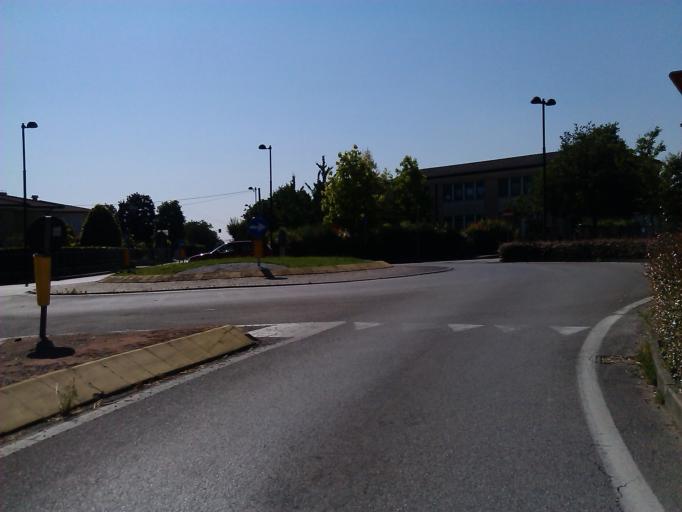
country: IT
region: Veneto
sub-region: Provincia di Vicenza
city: Cassola
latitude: 45.7514
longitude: 11.7928
